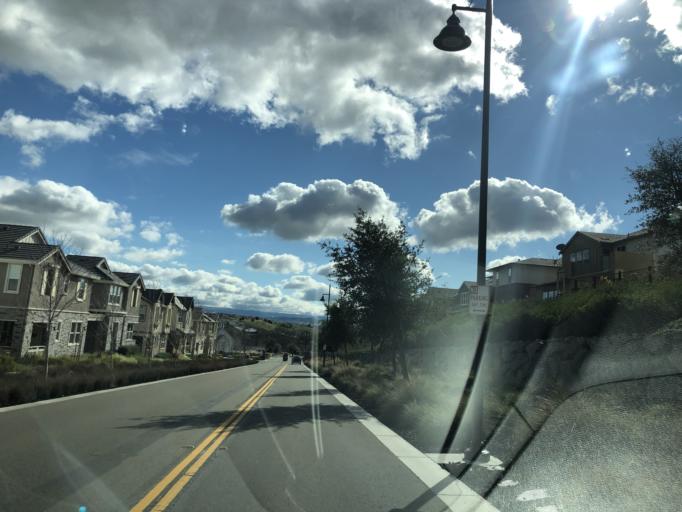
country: US
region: California
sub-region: Alameda County
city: Dublin
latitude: 37.7342
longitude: -121.8743
